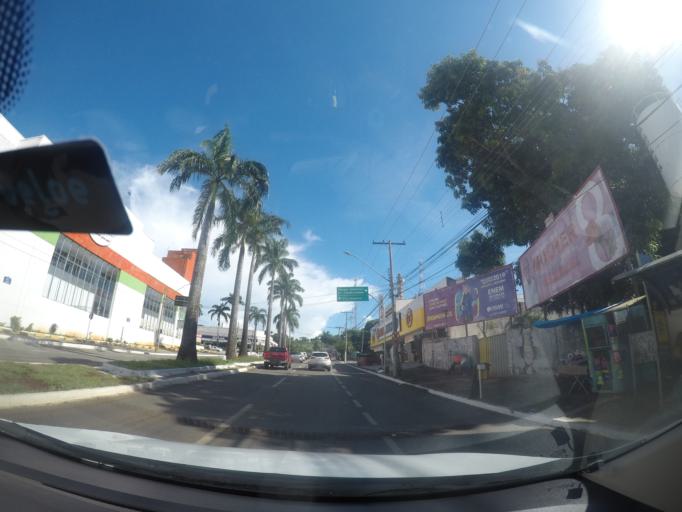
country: BR
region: Goias
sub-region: Goiania
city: Goiania
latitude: -16.7206
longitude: -49.2635
